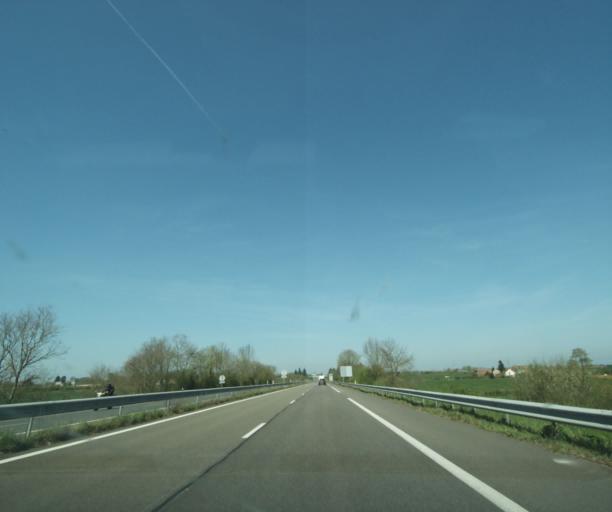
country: FR
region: Bourgogne
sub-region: Departement de la Nievre
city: La Charite-sur-Loire
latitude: 47.1784
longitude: 3.0425
